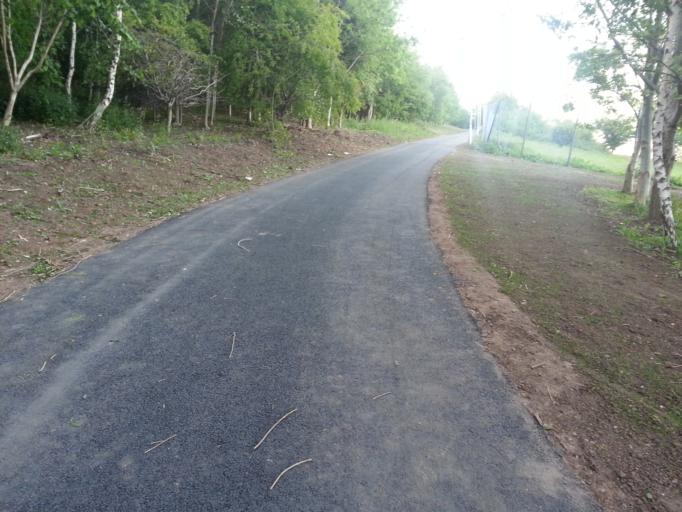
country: GB
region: Scotland
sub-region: West Lothian
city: Seafield
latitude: 55.9230
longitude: -3.1390
